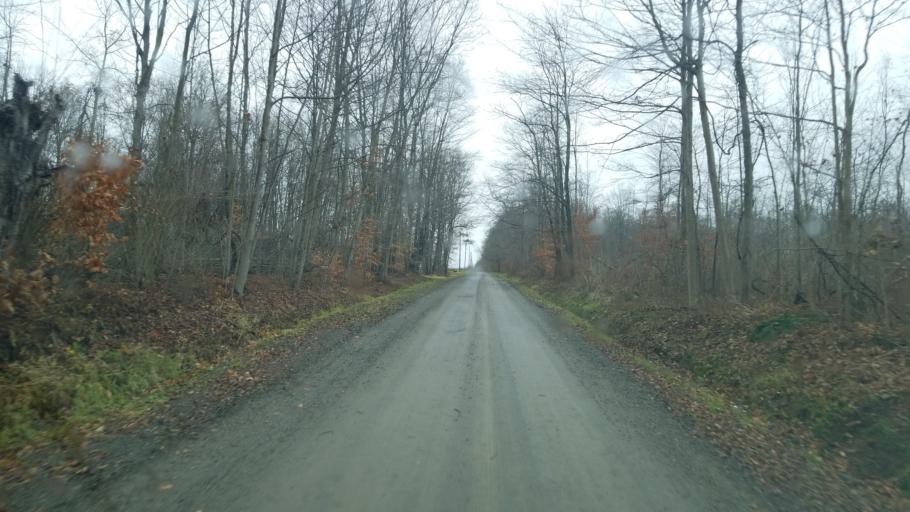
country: US
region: Ohio
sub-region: Ashtabula County
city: Roaming Shores
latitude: 41.6167
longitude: -80.7729
